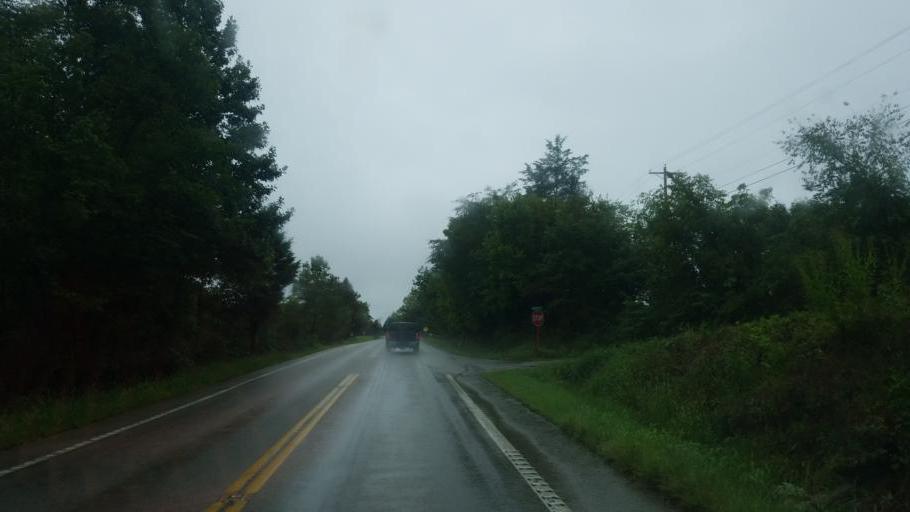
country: US
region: Ohio
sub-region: Adams County
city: West Union
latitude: 38.7988
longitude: -83.4696
